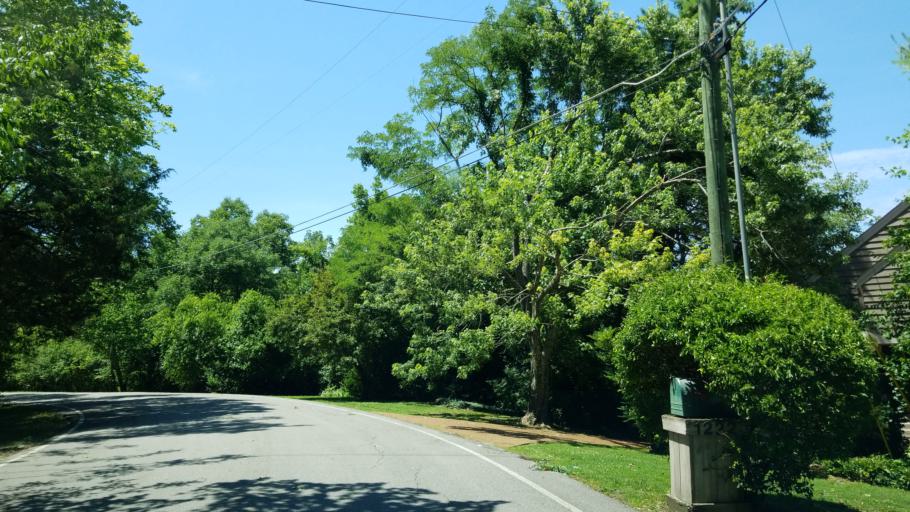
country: US
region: Tennessee
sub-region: Davidson County
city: Forest Hills
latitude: 36.0549
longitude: -86.8180
